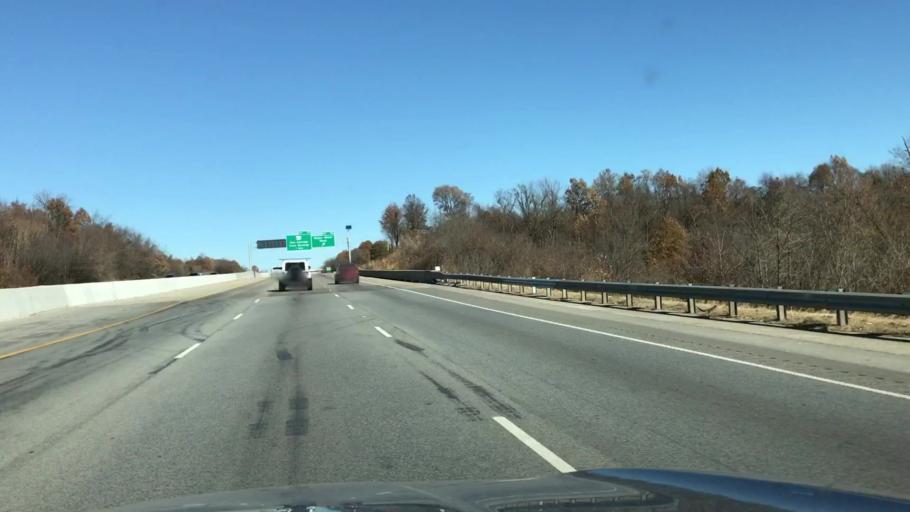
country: US
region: Arkansas
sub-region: Benton County
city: Bethel Heights
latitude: 36.2197
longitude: -94.1807
